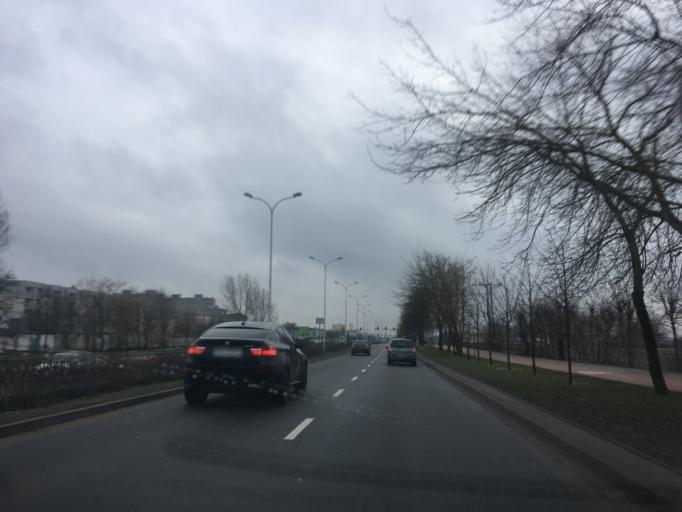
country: PL
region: Podlasie
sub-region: Suwalki
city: Suwalki
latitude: 54.1210
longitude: 22.9292
